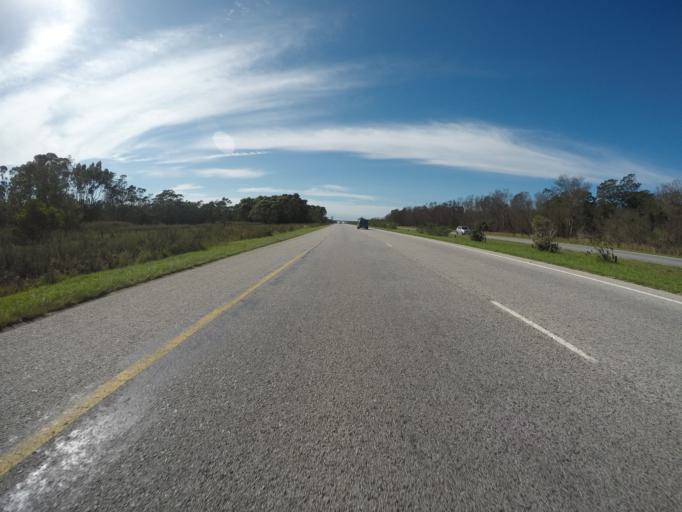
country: ZA
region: Eastern Cape
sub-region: Nelson Mandela Bay Metropolitan Municipality
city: Port Elizabeth
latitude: -33.9508
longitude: 25.4226
